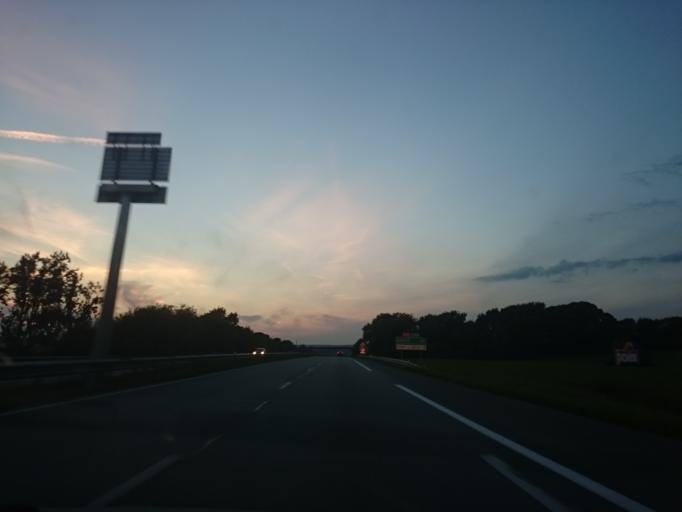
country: FR
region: Brittany
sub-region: Departement du Finistere
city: Chateaulin
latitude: 48.2175
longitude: -4.0571
